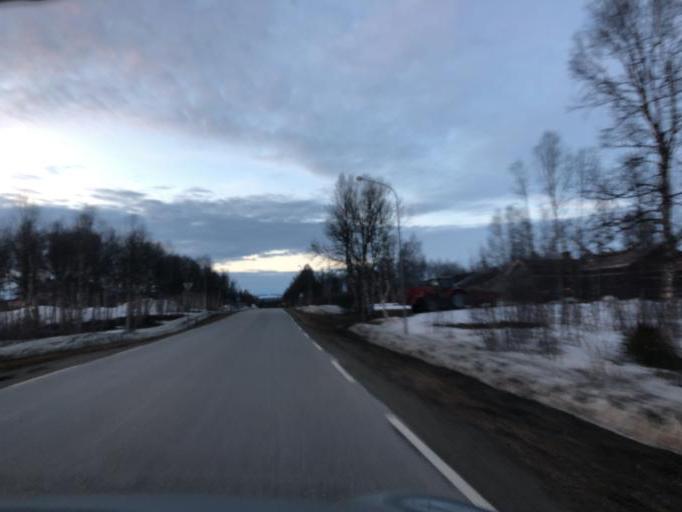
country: NO
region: Sor-Trondelag
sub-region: Tydal
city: Aas
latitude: 62.6471
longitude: 11.8653
